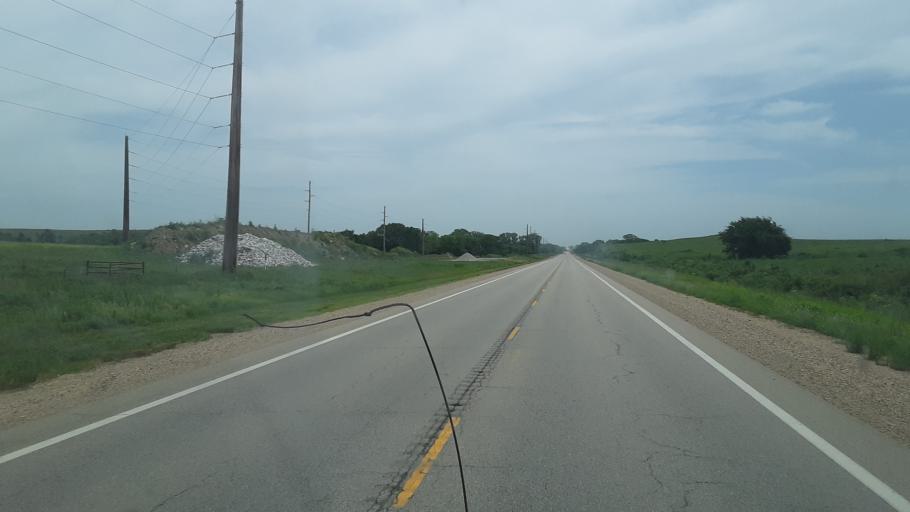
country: US
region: Kansas
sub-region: Woodson County
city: Yates Center
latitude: 37.8370
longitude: -95.9992
